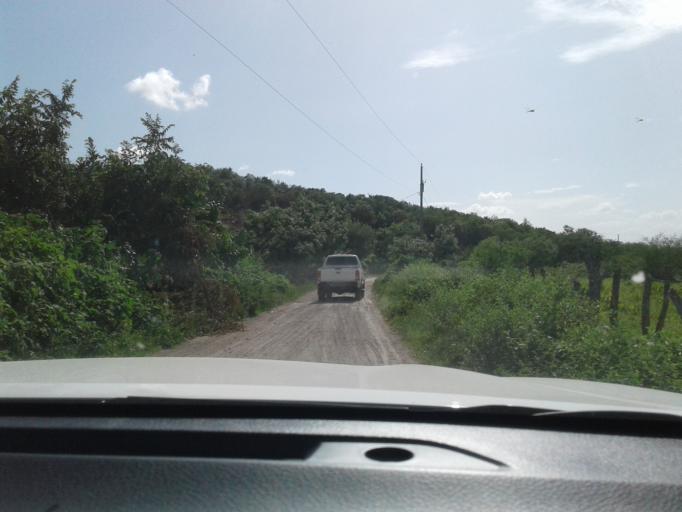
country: NI
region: Matagalpa
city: Terrabona
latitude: 12.5523
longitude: -86.0220
